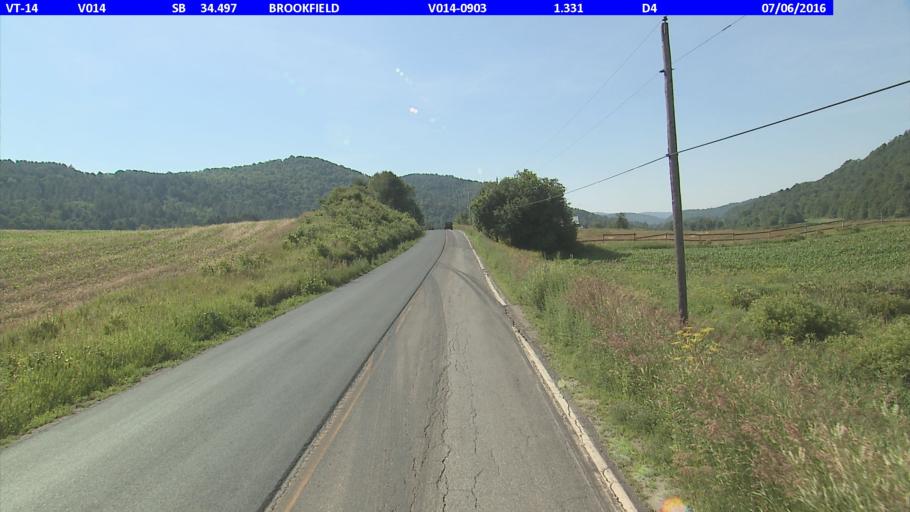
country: US
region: Vermont
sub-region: Orange County
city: Chelsea
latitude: 43.9978
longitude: -72.5592
